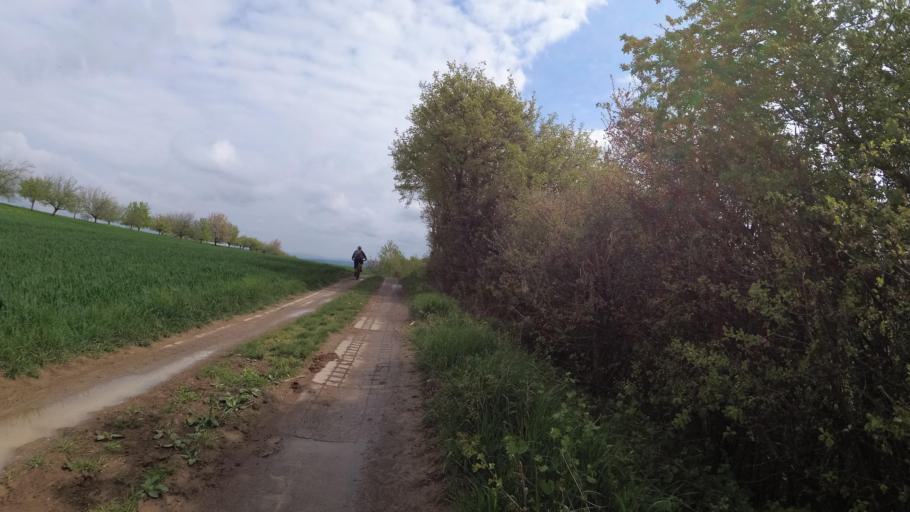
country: DE
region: Saarland
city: Merzig
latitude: 49.4066
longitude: 6.5879
